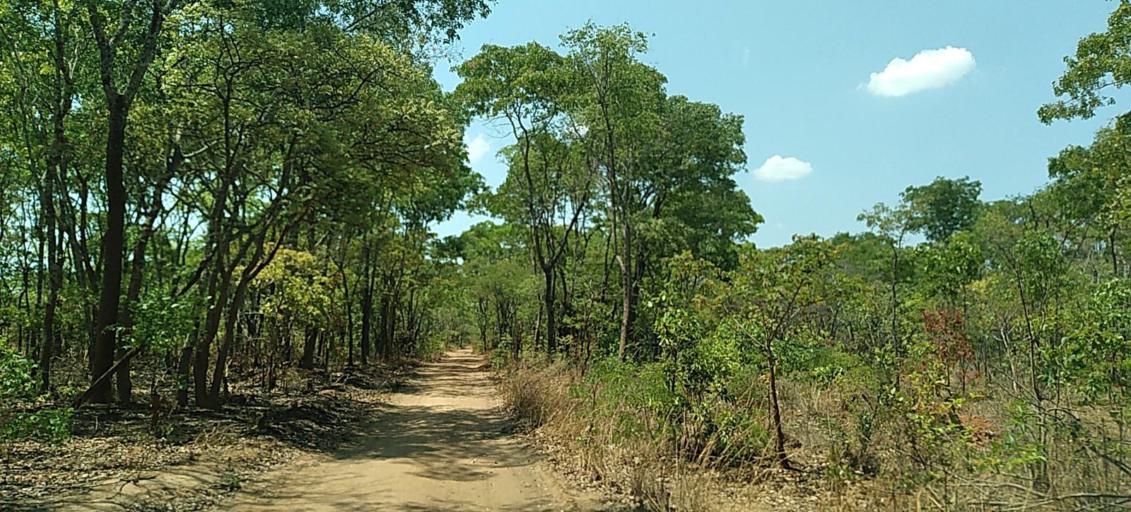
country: ZM
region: Copperbelt
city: Mpongwe
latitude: -13.6450
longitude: 28.4847
